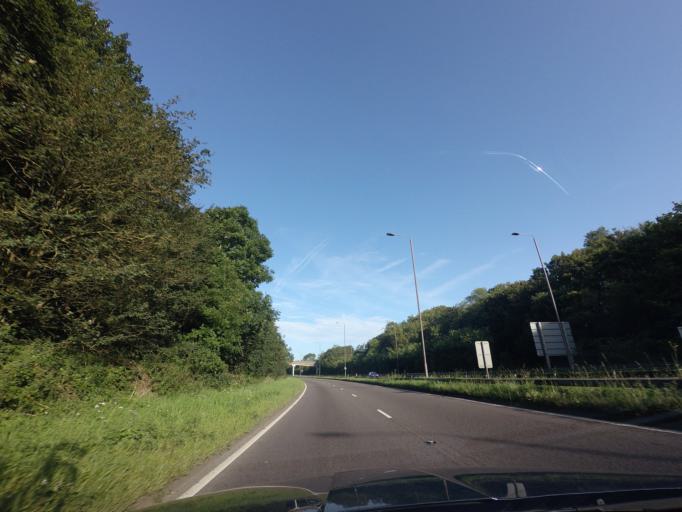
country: GB
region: England
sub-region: Derbyshire
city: Bolsover
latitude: 53.1995
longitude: -1.3278
